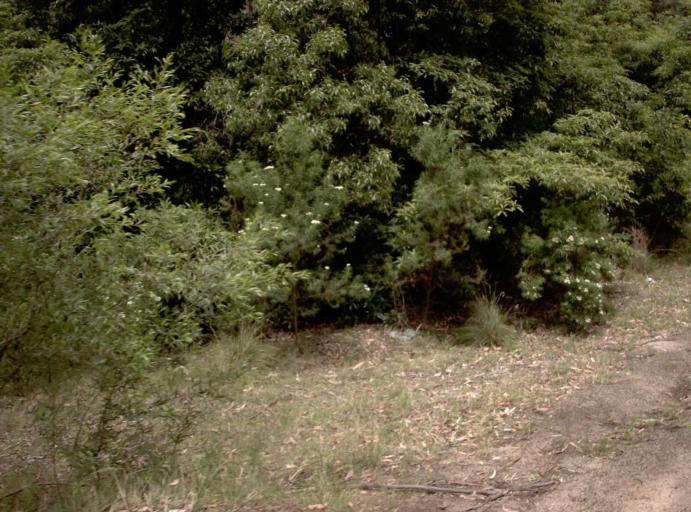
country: AU
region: Victoria
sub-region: Latrobe
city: Traralgon
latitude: -38.4297
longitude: 146.7413
